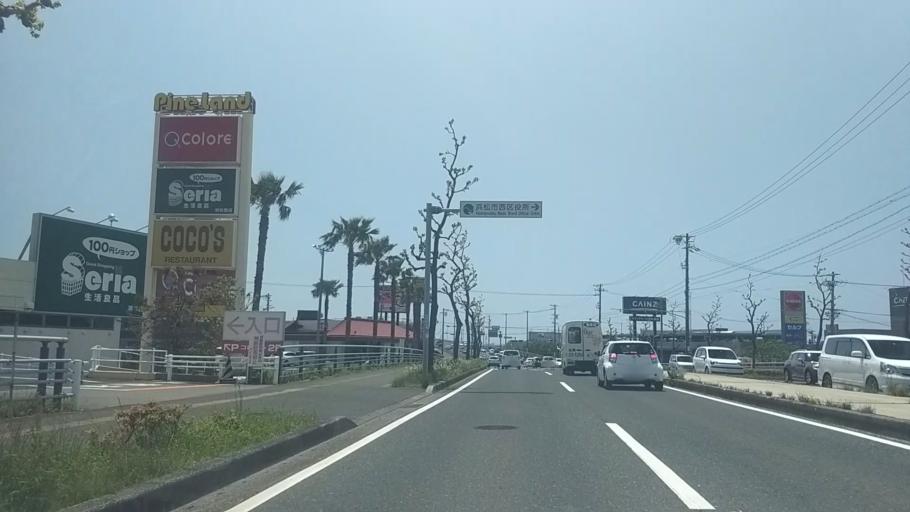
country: JP
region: Shizuoka
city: Hamamatsu
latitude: 34.6967
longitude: 137.6482
